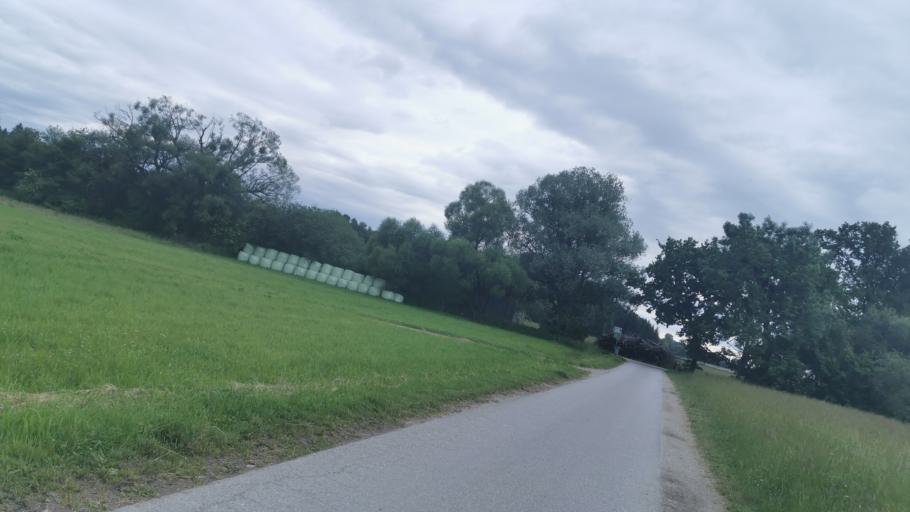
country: DE
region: Bavaria
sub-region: Upper Bavaria
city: Piding
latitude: 47.7657
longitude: 12.9669
